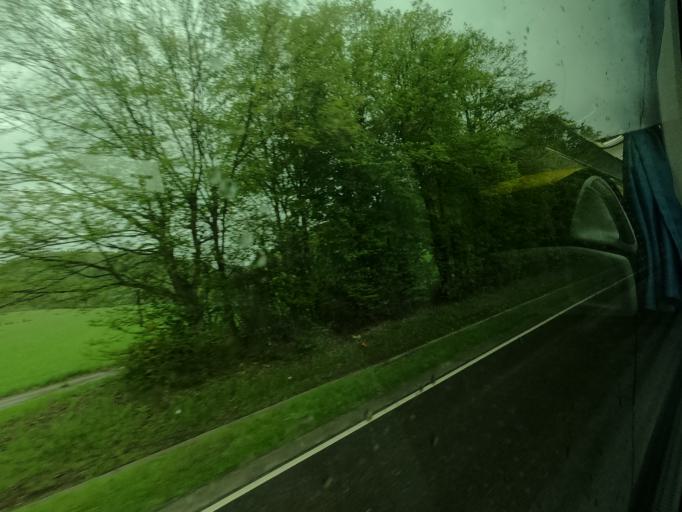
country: DE
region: Baden-Wuerttemberg
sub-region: Regierungsbezirk Stuttgart
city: Oberkochen
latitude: 48.7878
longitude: 10.1260
